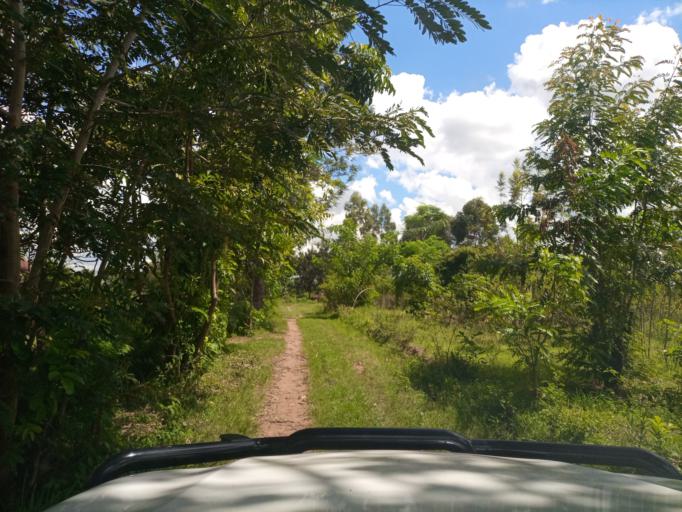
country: UG
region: Eastern Region
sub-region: Tororo District
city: Tororo
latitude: 0.7225
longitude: 34.0216
